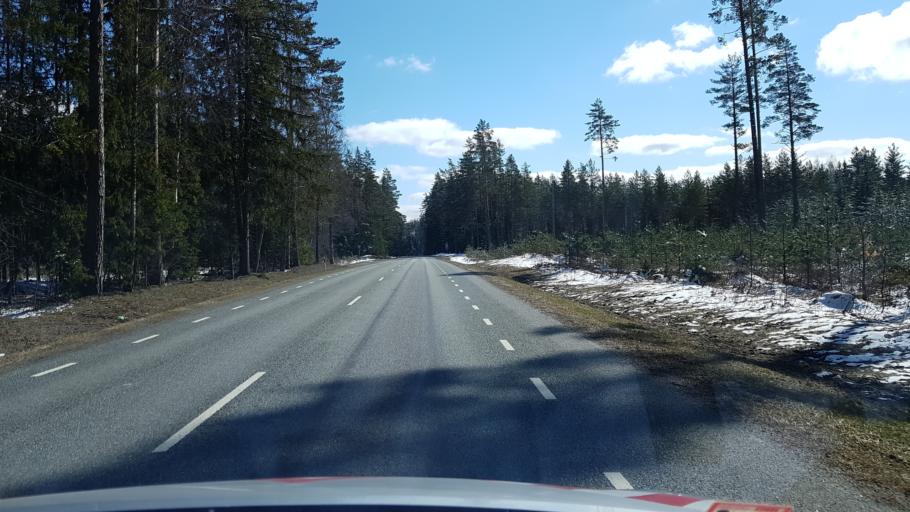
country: EE
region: Laeaene-Virumaa
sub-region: Tapa vald
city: Tapa
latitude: 59.4299
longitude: 25.9745
